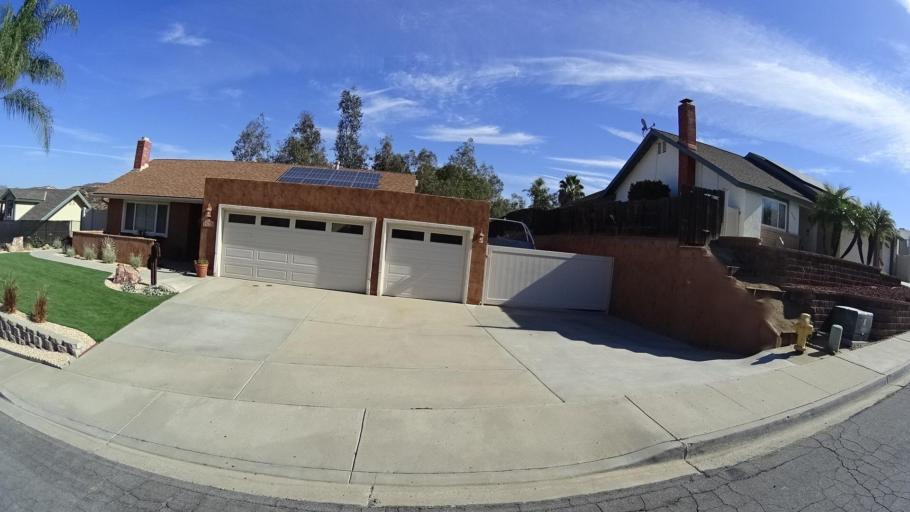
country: US
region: California
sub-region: San Diego County
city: Lakeside
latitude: 32.8382
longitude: -116.9126
